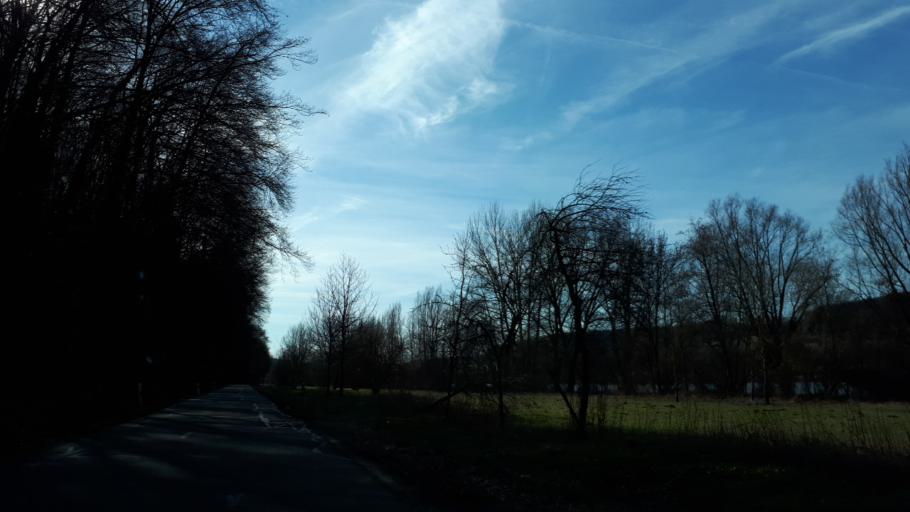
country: DE
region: Bavaria
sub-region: Upper Palatinate
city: Pentling
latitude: 48.9795
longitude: 12.0416
